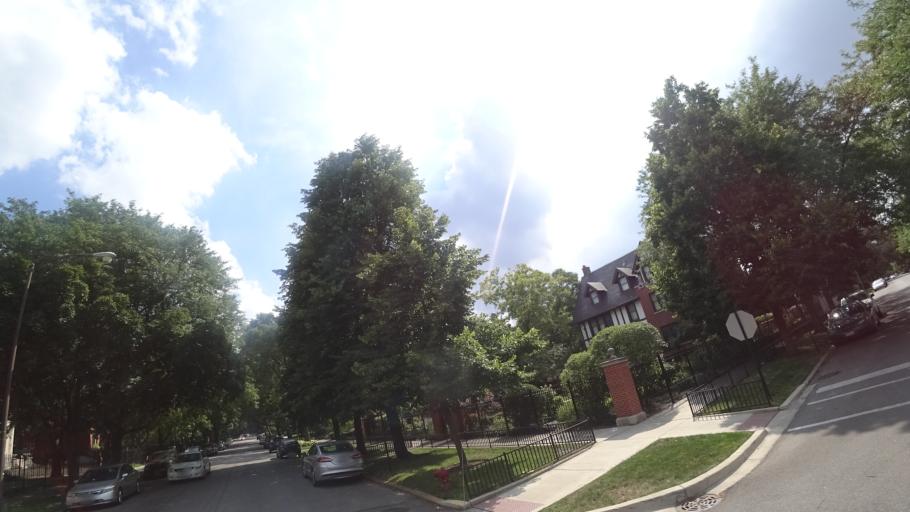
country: US
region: Illinois
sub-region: Cook County
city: Chicago
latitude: 41.8078
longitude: -87.5969
